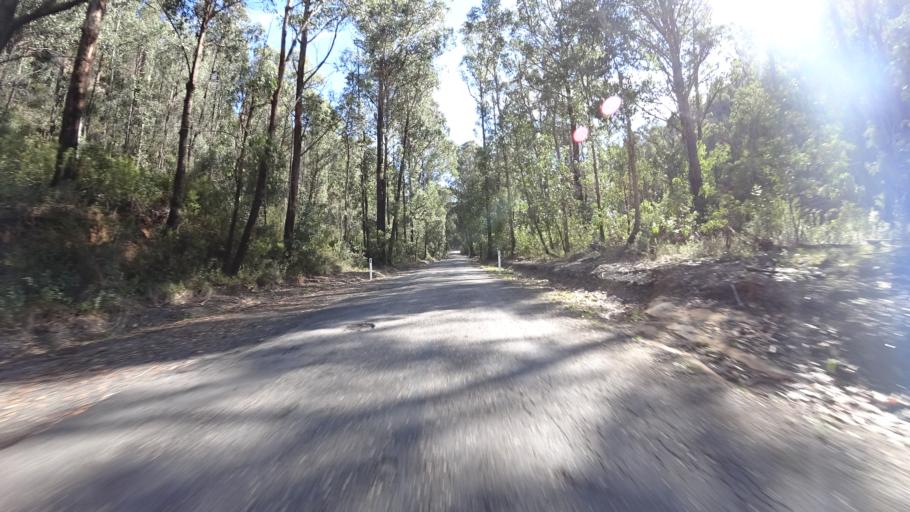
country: AU
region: New South Wales
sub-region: Lithgow
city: Lithgow
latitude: -33.4500
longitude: 150.1756
